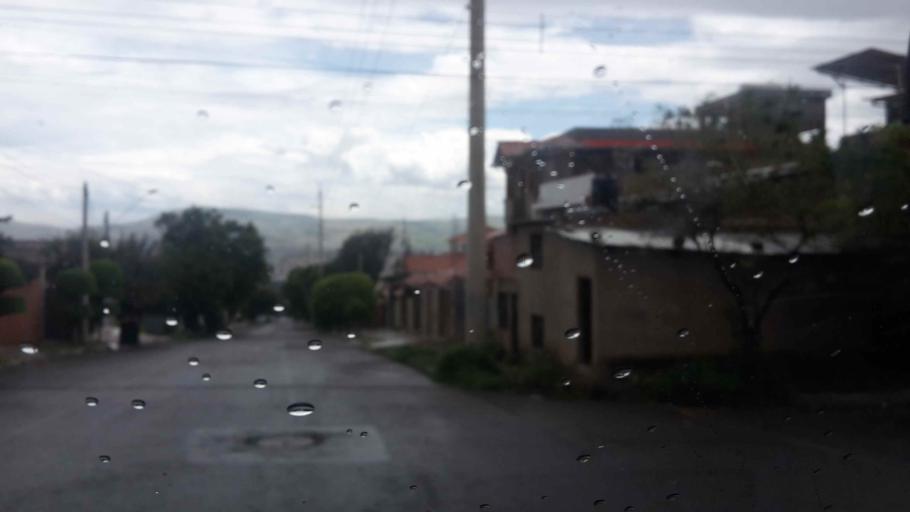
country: BO
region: Cochabamba
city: Cochabamba
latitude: -17.3622
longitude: -66.1595
